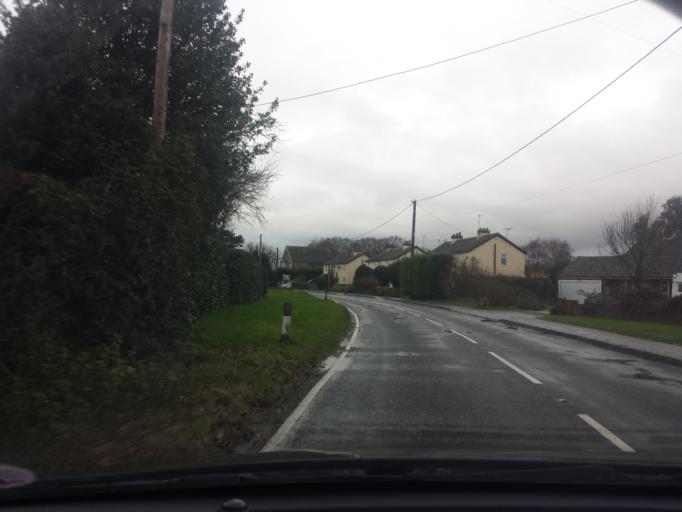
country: GB
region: England
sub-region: Essex
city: Little Clacton
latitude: 51.8744
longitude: 1.1223
